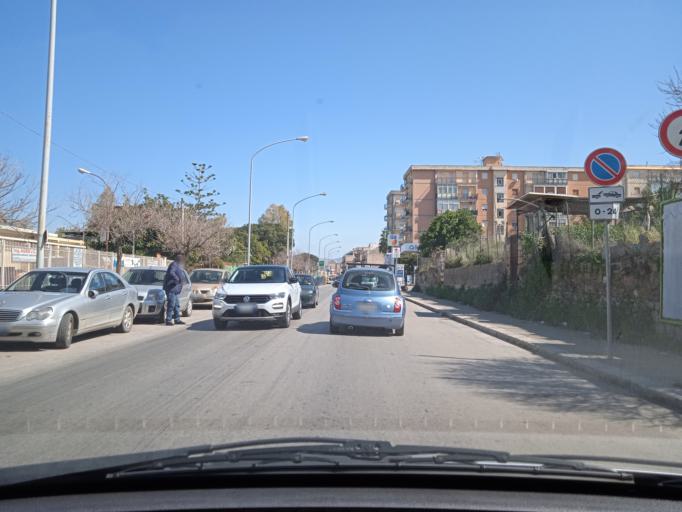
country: IT
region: Sicily
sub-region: Palermo
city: Ciaculli
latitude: 38.1016
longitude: 13.3984
